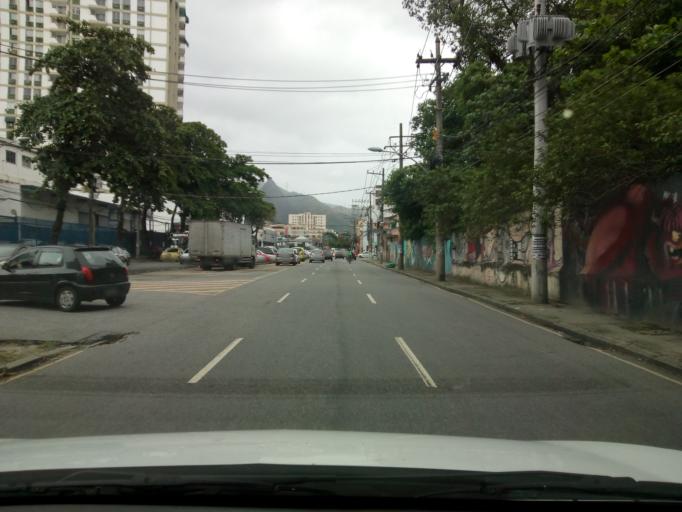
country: BR
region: Rio de Janeiro
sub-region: Rio De Janeiro
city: Rio de Janeiro
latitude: -22.9162
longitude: -43.2384
